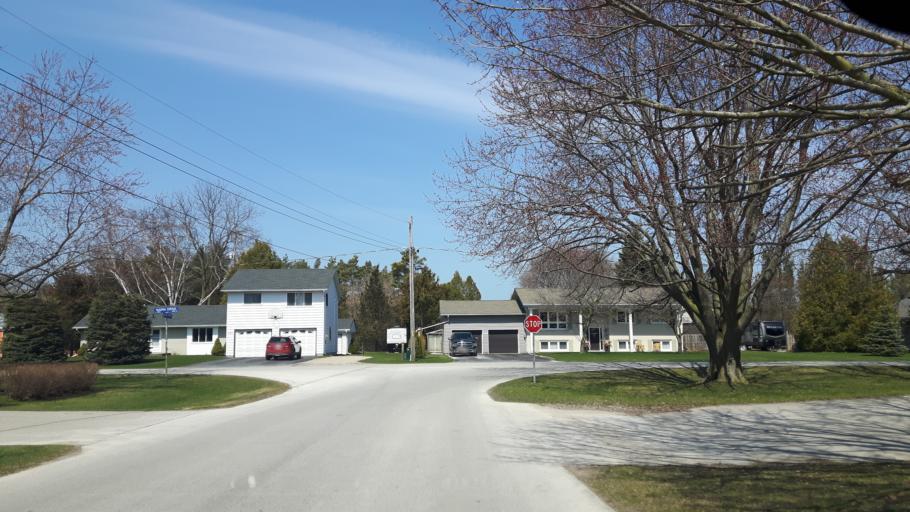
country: CA
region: Ontario
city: Goderich
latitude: 43.7264
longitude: -81.6865
